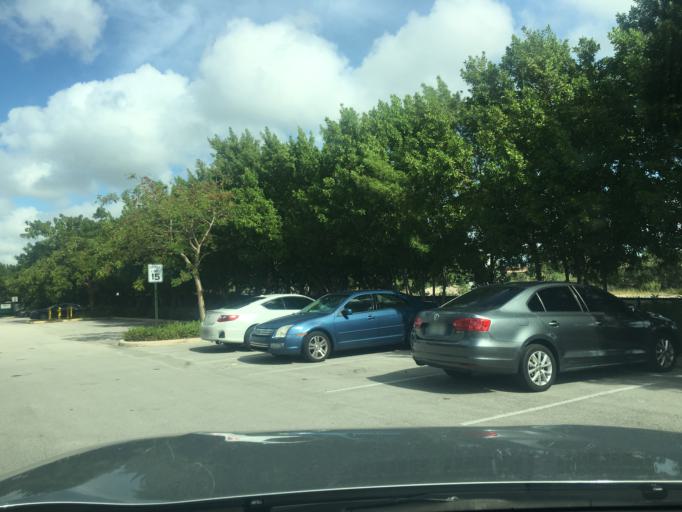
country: US
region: Florida
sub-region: Broward County
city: Broadview Park
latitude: 26.0800
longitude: -80.1775
